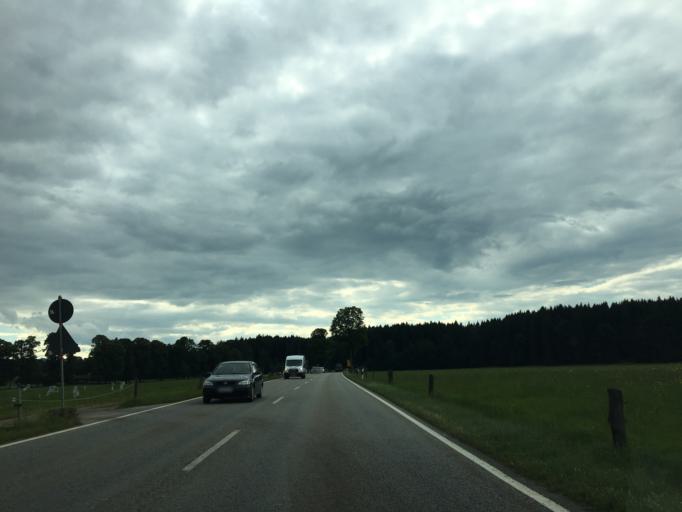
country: DE
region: Bavaria
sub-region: Upper Bavaria
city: Gmund am Tegernsee
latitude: 47.7772
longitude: 11.7638
